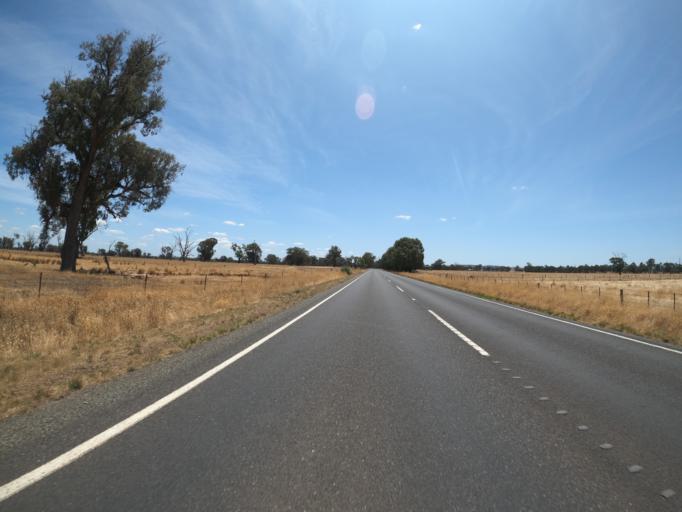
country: AU
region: Victoria
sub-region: Benalla
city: Benalla
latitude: -36.5109
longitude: 146.0286
